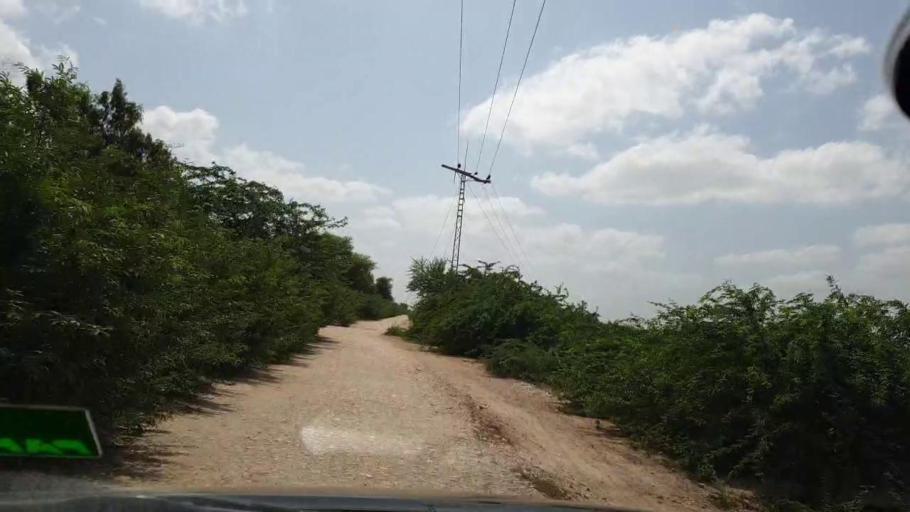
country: PK
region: Sindh
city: Kadhan
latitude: 24.5521
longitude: 69.2113
